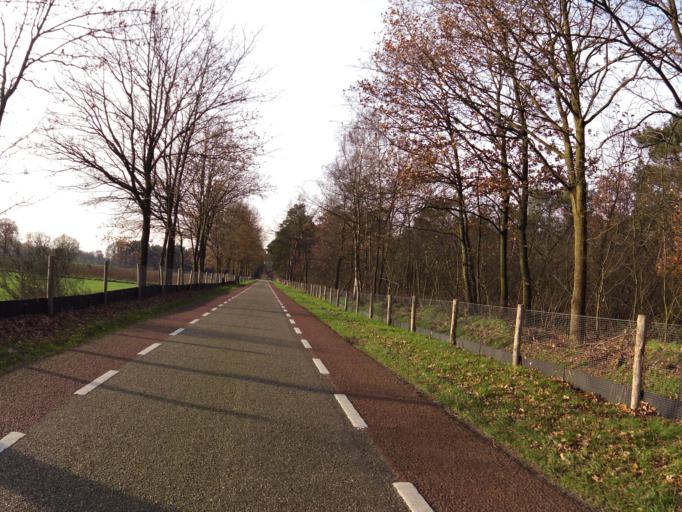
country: NL
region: North Brabant
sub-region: Gemeente Uden
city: Odiliapeel
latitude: 51.6699
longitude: 5.6974
